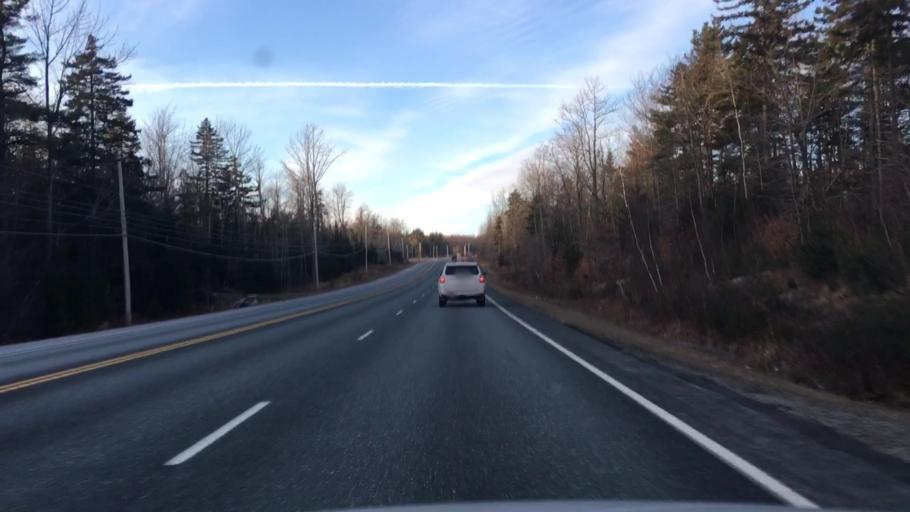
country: US
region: Maine
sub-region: Hancock County
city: Dedham
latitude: 44.6398
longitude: -68.5509
